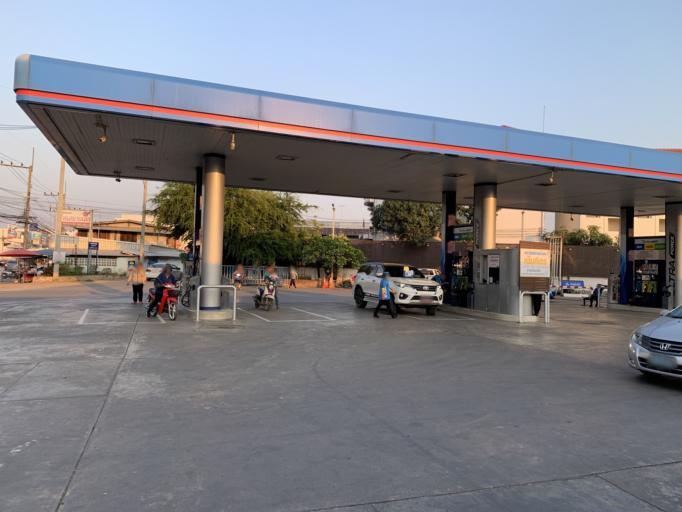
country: TH
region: Loei
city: Loei
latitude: 17.4874
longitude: 101.7268
